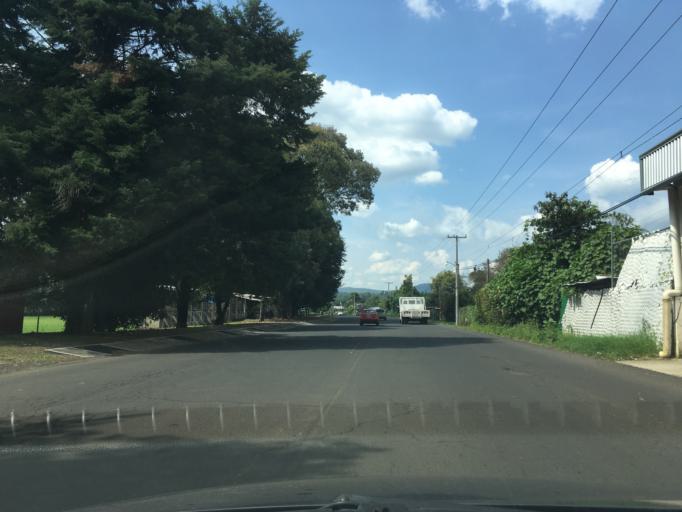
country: MX
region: Michoacan
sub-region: Tingueindin
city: Tingueindin
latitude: 19.7690
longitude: -102.4966
